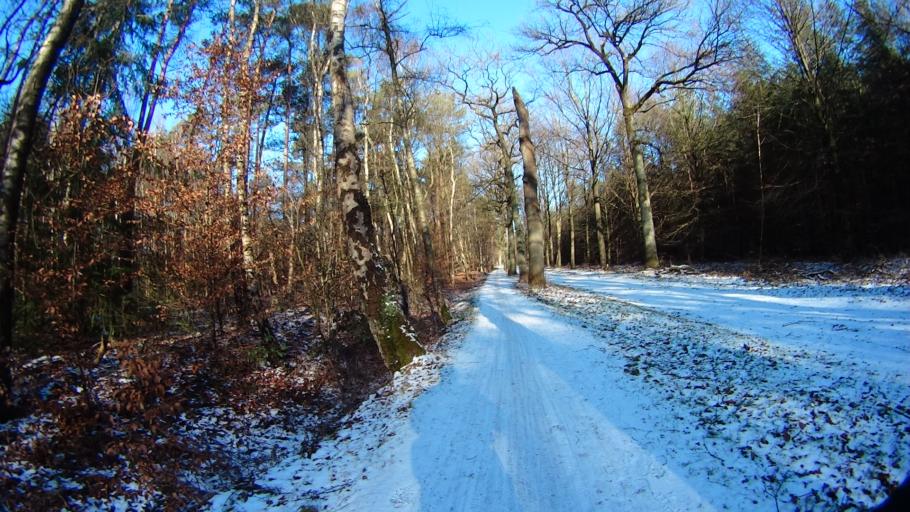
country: NL
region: North Holland
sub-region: Gemeente Hilversum
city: Hilversum
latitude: 52.2116
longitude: 5.2188
